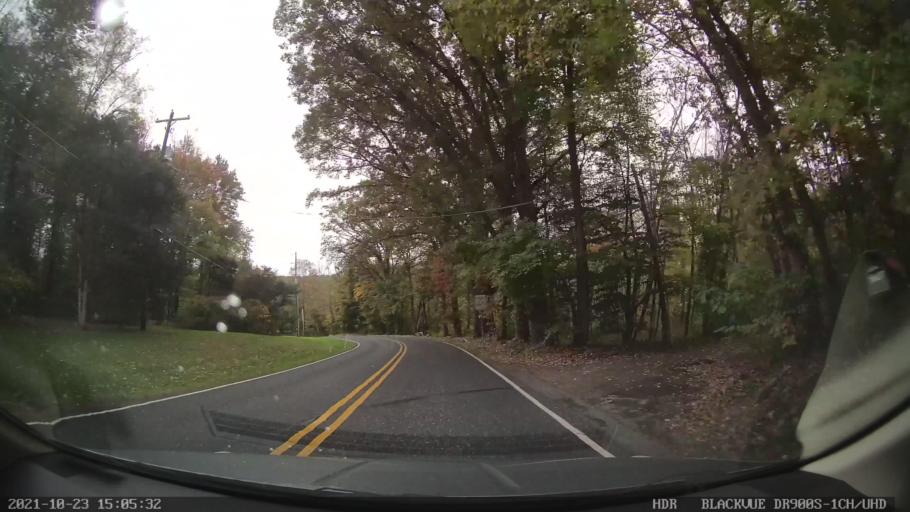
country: US
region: Pennsylvania
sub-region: Berks County
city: Bally
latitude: 40.4321
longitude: -75.5815
